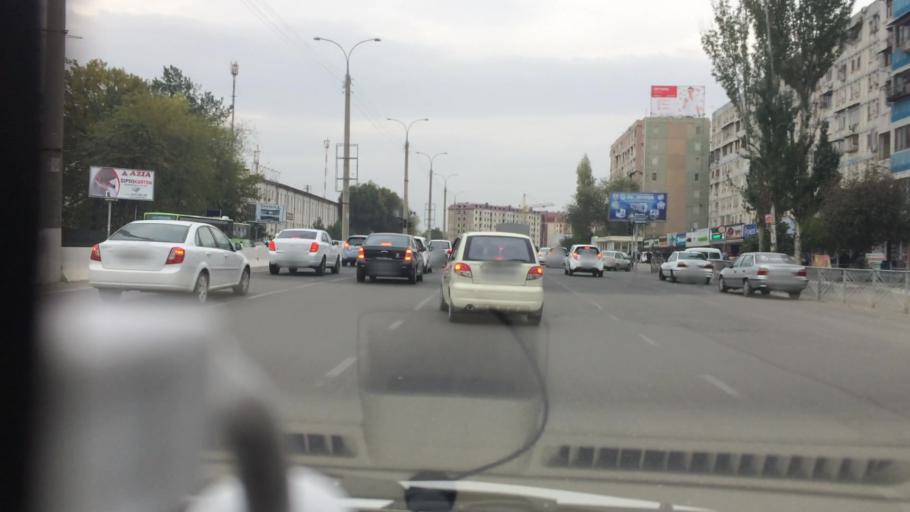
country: UZ
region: Toshkent
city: Salor
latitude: 41.3151
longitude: 69.3243
